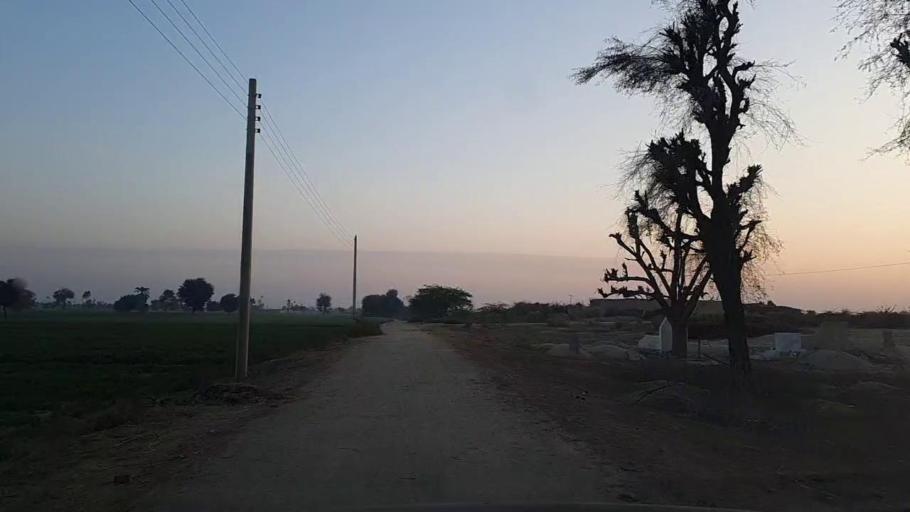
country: PK
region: Sindh
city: Jam Sahib
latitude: 26.4598
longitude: 68.5215
